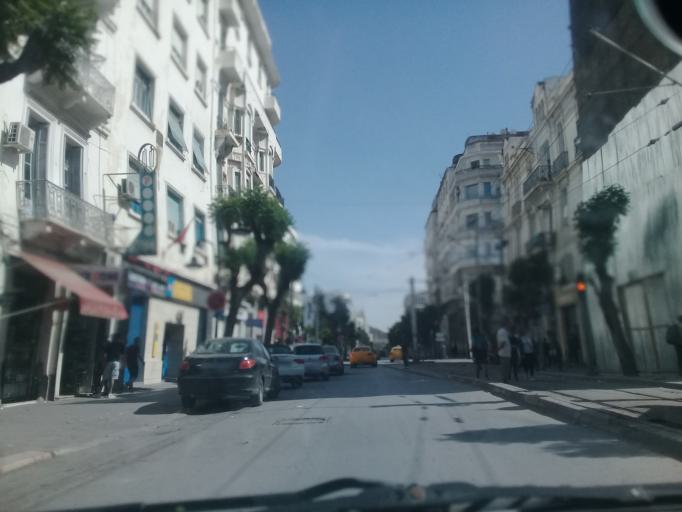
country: TN
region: Tunis
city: Tunis
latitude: 36.7981
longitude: 10.1816
